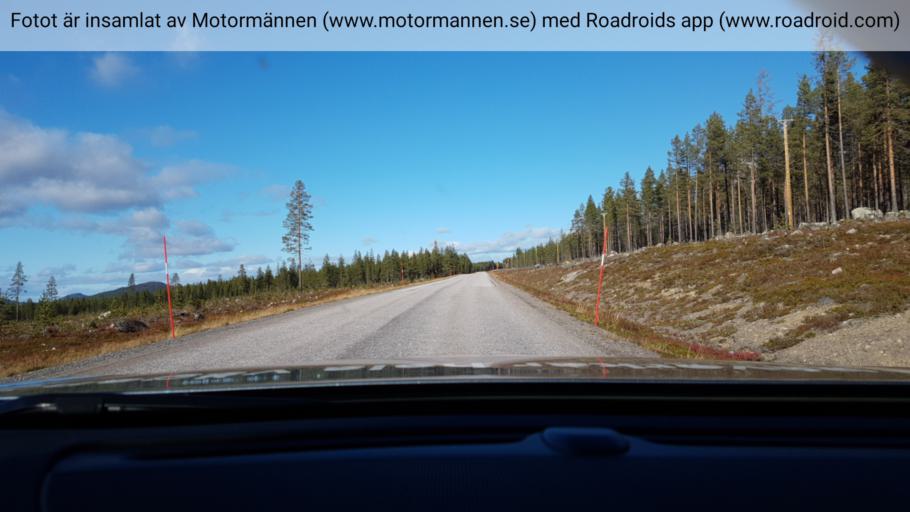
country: SE
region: Vaesterbotten
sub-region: Mala Kommun
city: Mala
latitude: 65.7769
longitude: 18.5147
